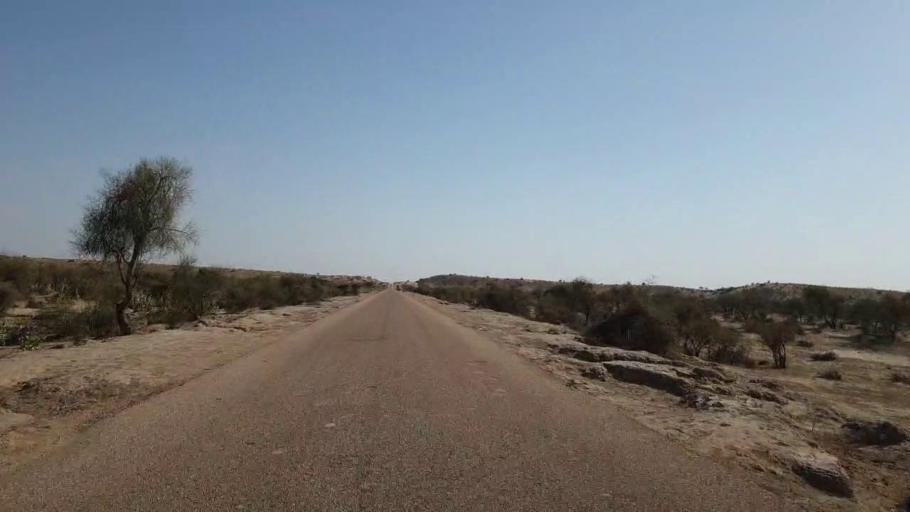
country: PK
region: Sindh
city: Nabisar
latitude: 25.0886
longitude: 70.0406
